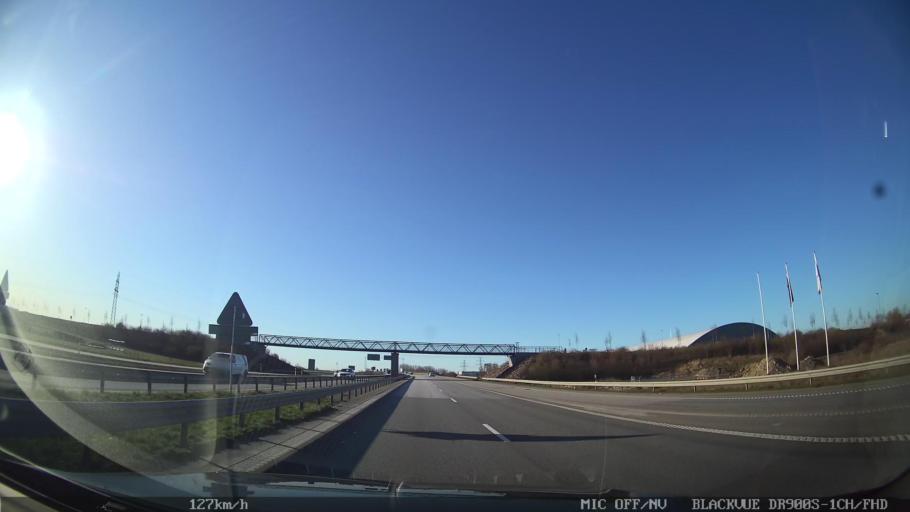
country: SE
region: Skane
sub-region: Landskrona
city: Landskrona
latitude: 55.8720
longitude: 12.8787
